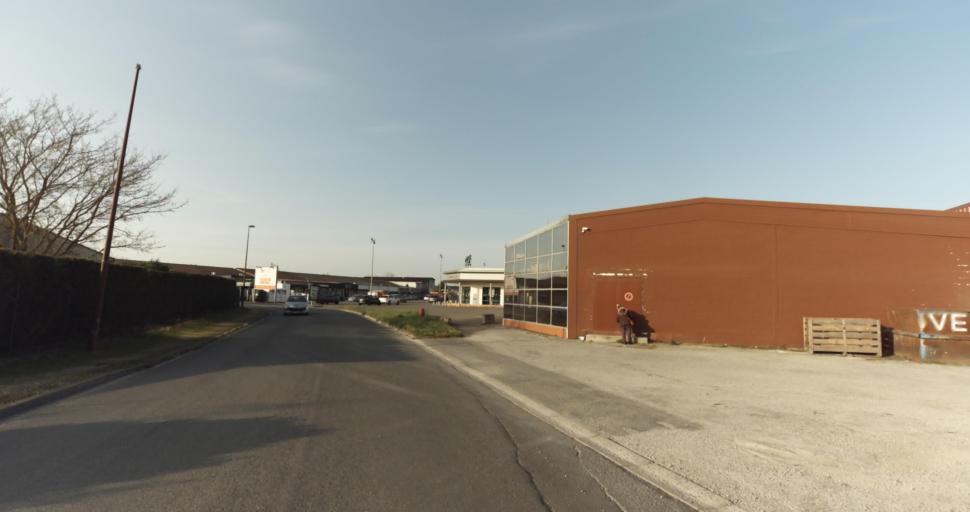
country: FR
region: Midi-Pyrenees
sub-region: Departement du Tarn
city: Saint-Sulpice-la-Pointe
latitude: 43.7731
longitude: 1.6774
